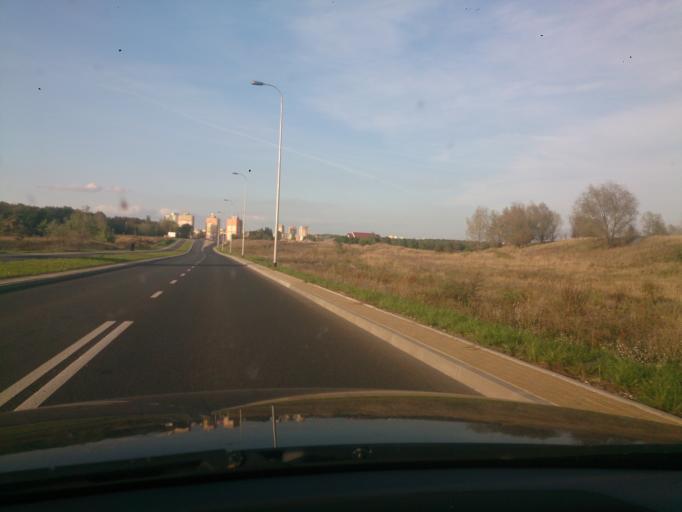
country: PL
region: Kujawsko-Pomorskie
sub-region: Grudziadz
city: Grudziadz
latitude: 53.4441
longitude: 18.7148
